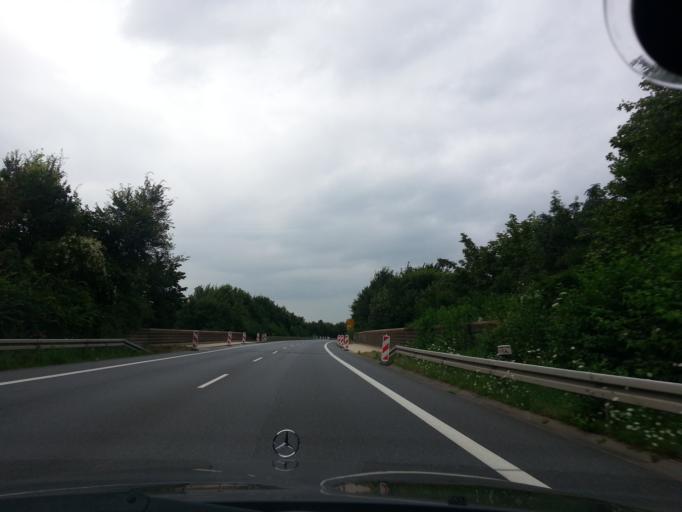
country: DE
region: North Rhine-Westphalia
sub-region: Regierungsbezirk Munster
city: Borken
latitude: 51.8394
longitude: 6.8365
